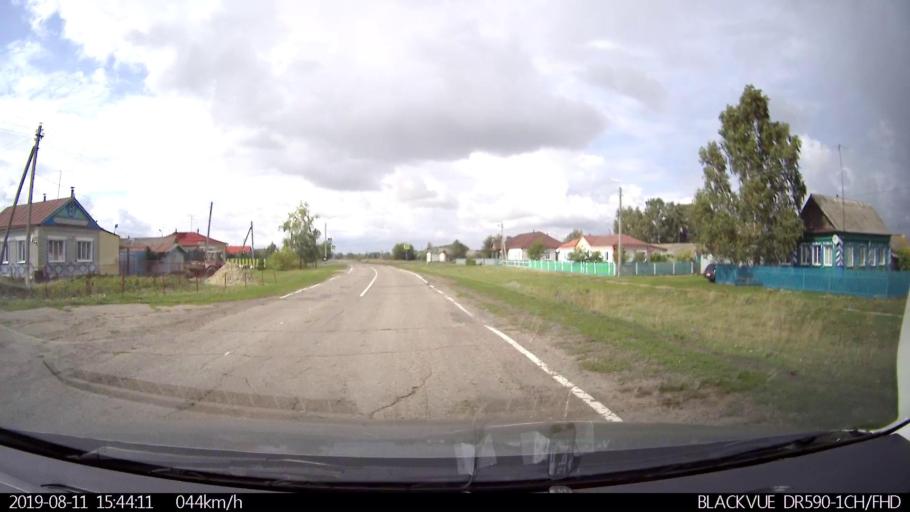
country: RU
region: Ulyanovsk
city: Ignatovka
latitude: 53.8806
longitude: 47.6575
